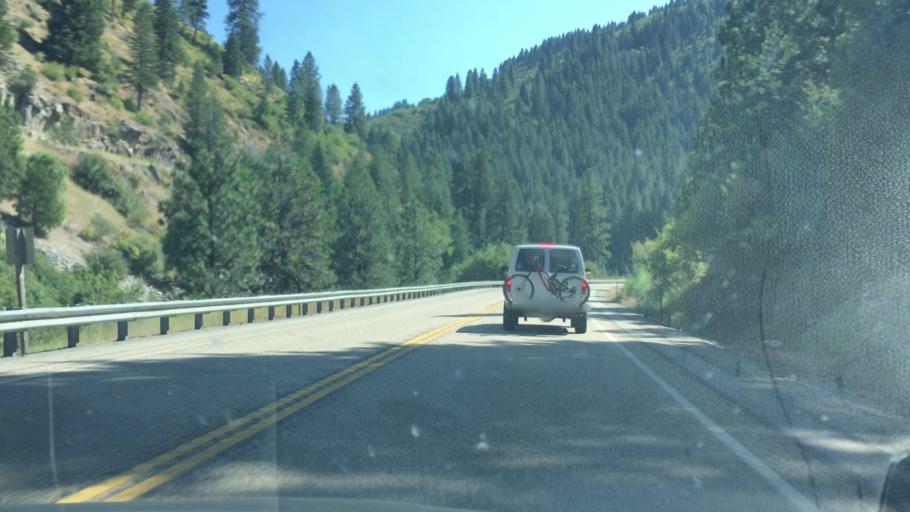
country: US
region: Idaho
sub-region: Valley County
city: Cascade
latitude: 44.1224
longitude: -116.1109
